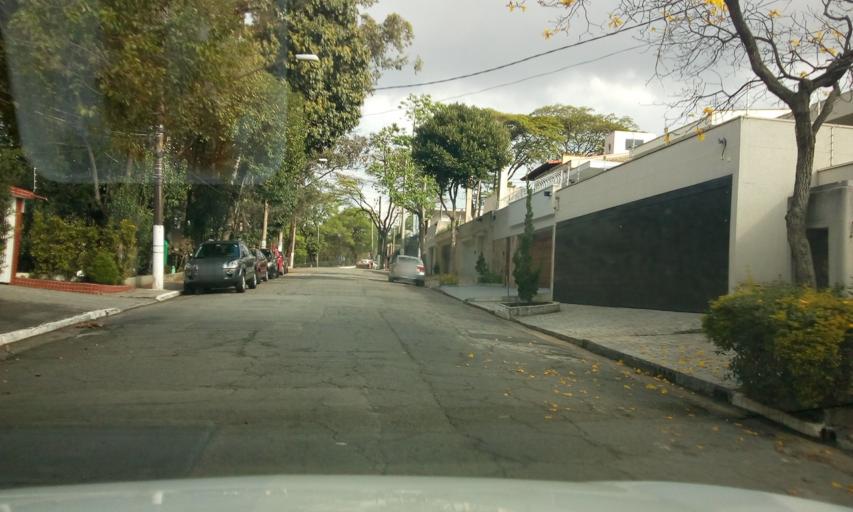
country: BR
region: Sao Paulo
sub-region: Sao Paulo
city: Sao Paulo
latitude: -23.6032
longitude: -46.6521
